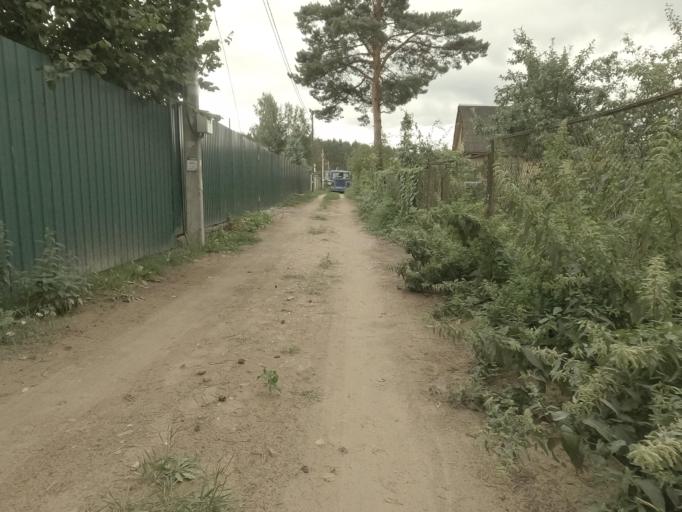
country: RU
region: Leningrad
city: Kirovsk
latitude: 59.8968
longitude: 31.0069
